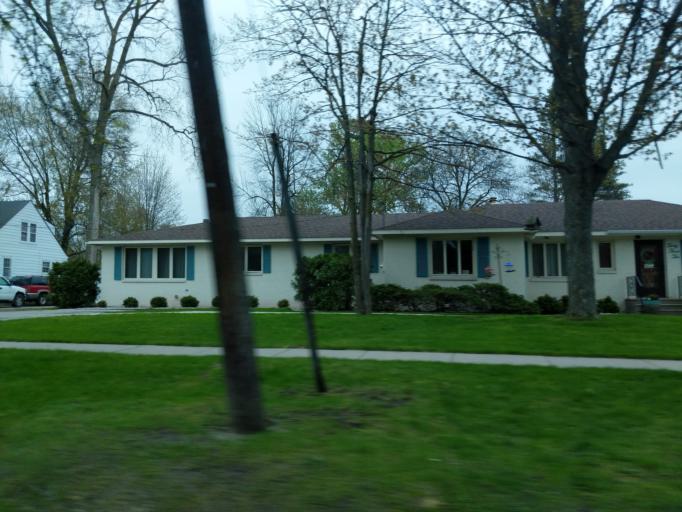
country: US
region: Michigan
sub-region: Midland County
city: Midland
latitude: 43.6289
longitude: -84.2270
